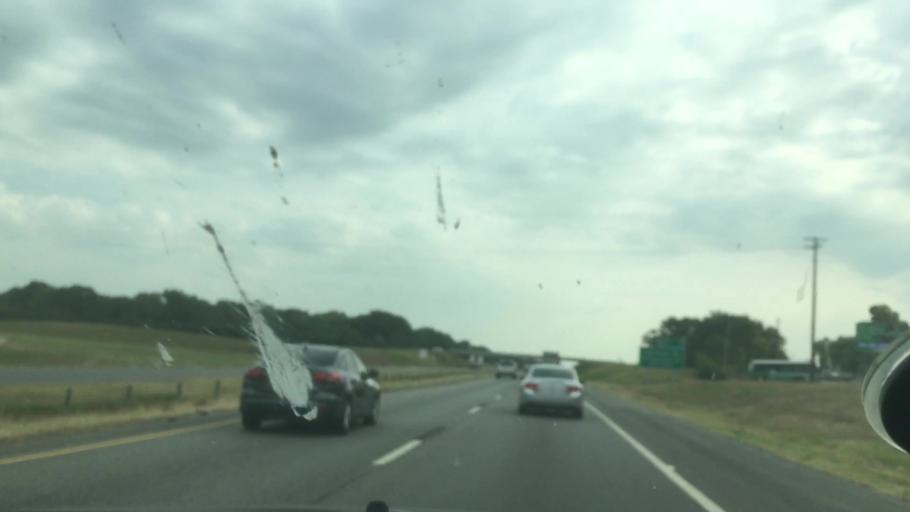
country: US
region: Oklahoma
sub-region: Bryan County
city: Colbert
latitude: 33.8280
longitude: -96.5290
